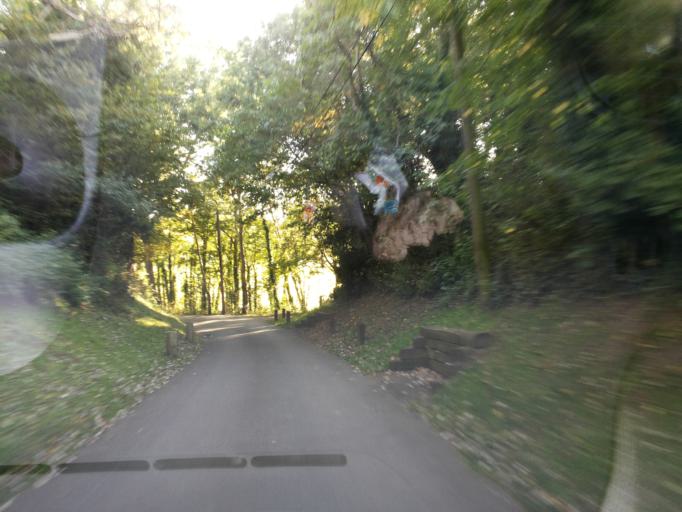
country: GB
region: England
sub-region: Worcestershire
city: Stourport-on-Severn
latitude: 52.3467
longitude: -2.2978
